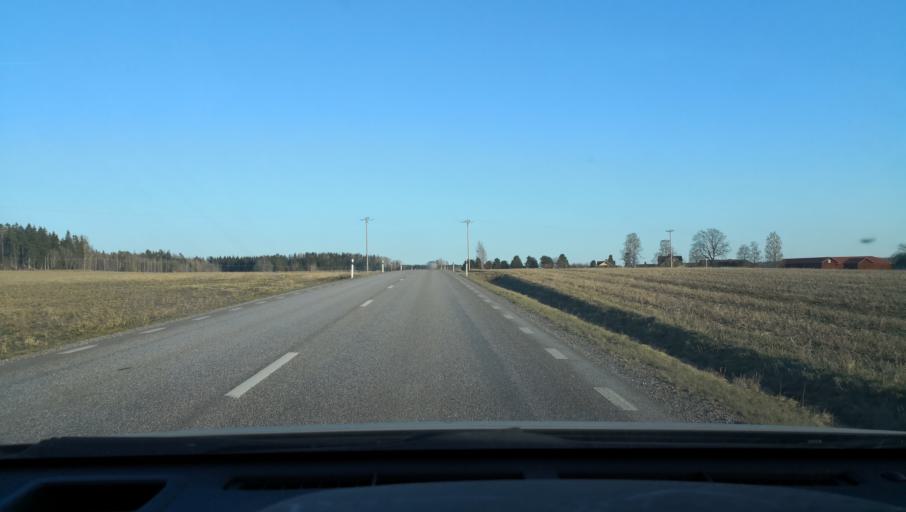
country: SE
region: Uppsala
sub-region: Heby Kommun
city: Heby
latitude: 59.9317
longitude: 16.8722
